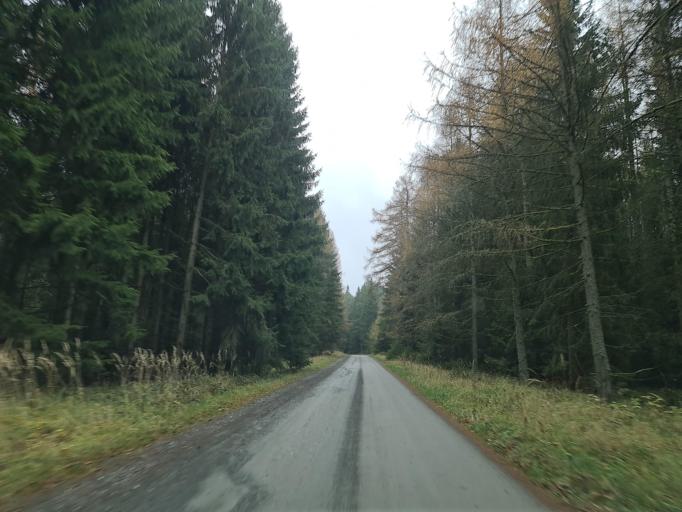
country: DE
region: Saxony
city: Mehltheuer
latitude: 50.5245
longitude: 12.0468
